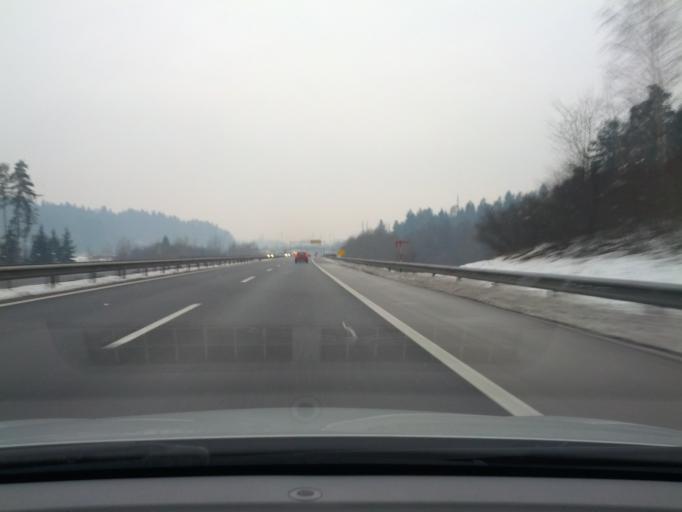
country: SI
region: Domzale
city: Dob
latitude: 46.1375
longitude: 14.6222
